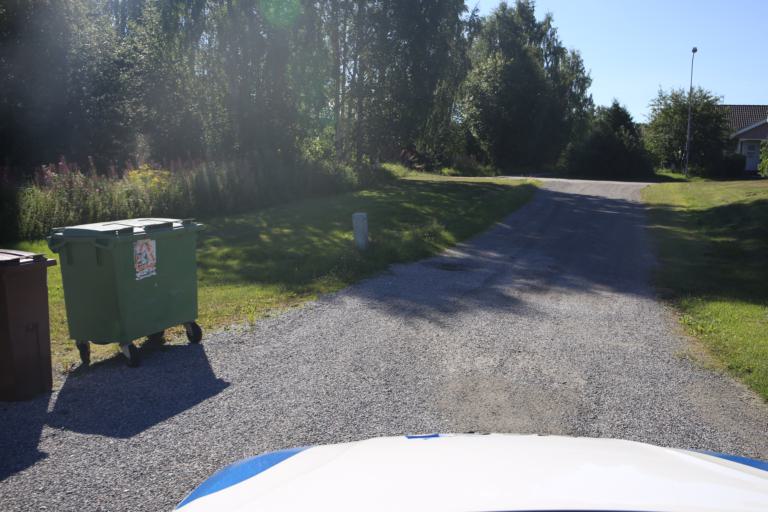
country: SE
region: Vaesterbotten
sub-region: Skelleftea Kommun
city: Viken
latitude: 64.7475
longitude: 20.7728
